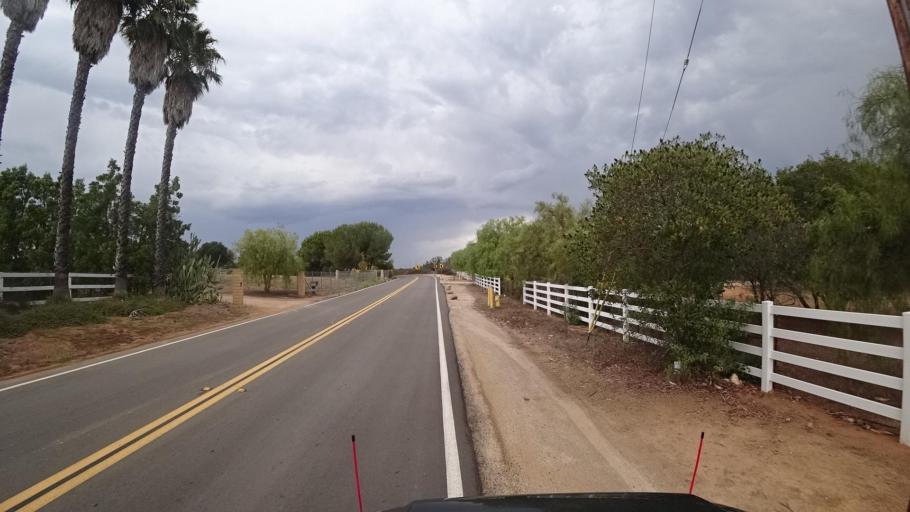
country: US
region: California
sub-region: San Diego County
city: San Pasqual
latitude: 33.0335
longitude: -116.9739
